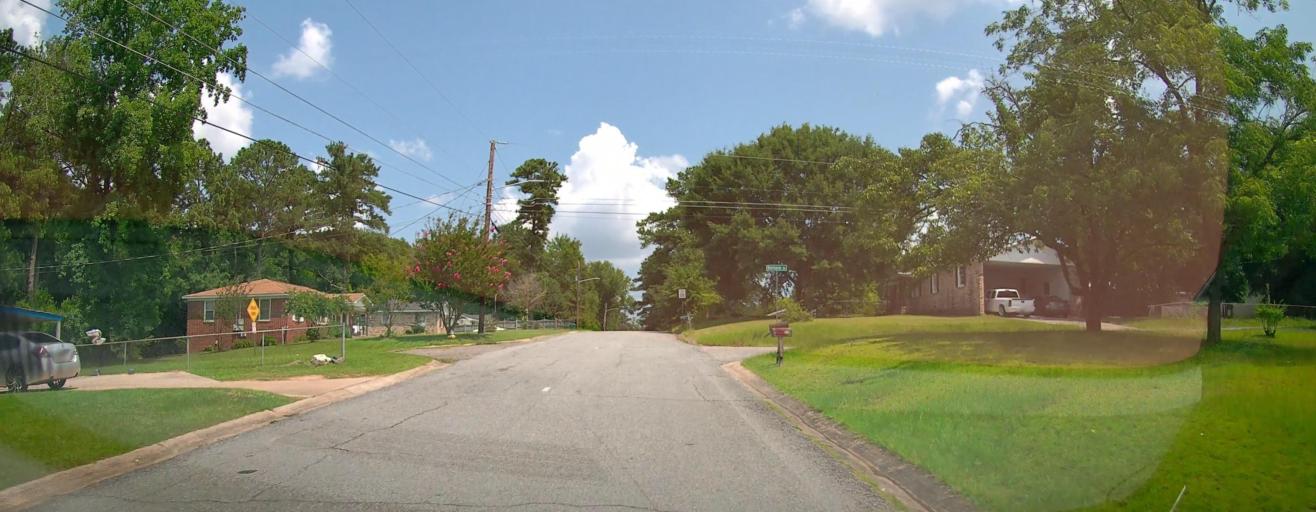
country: US
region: Georgia
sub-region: Bibb County
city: West Point
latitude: 32.8178
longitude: -83.7215
